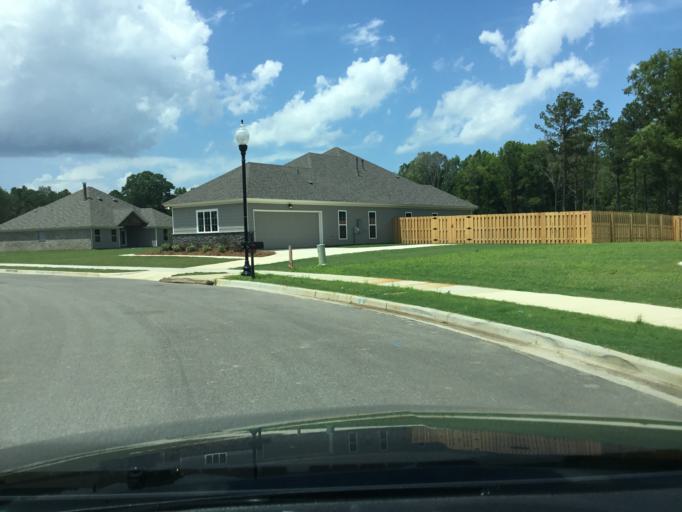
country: US
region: Alabama
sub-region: Montgomery County
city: Pike Road
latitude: 32.3343
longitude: -86.0707
